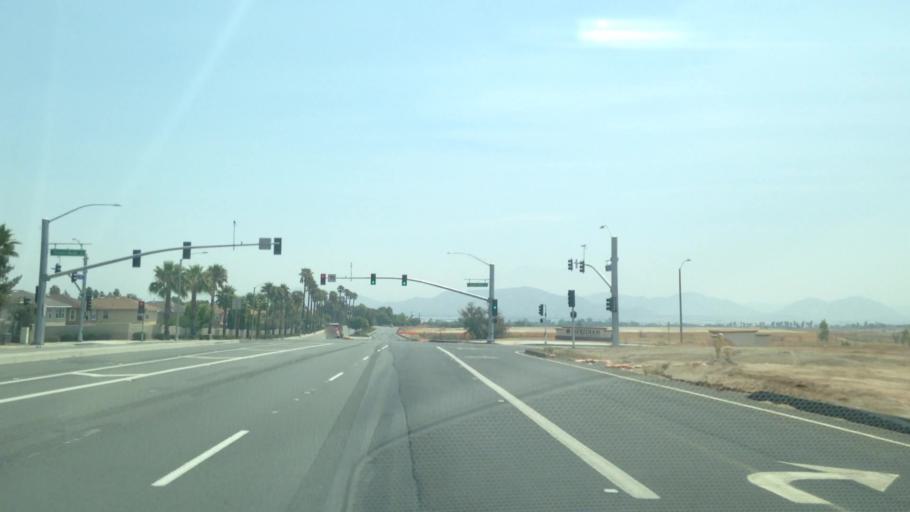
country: US
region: California
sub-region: Riverside County
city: March Air Force Base
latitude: 33.8875
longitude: -117.3083
